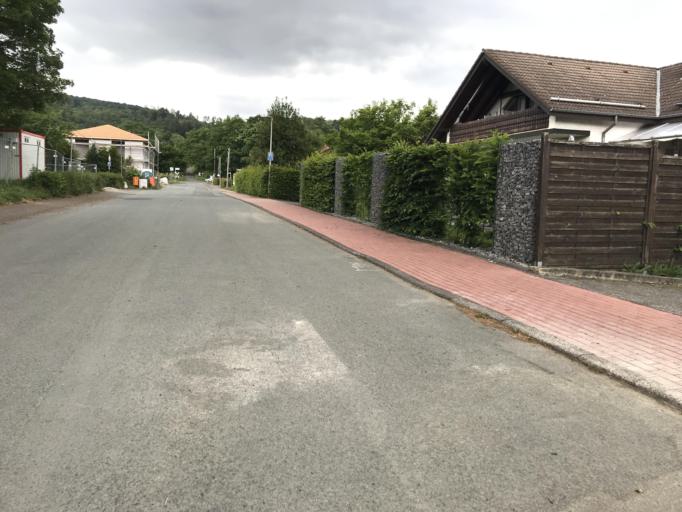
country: DE
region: Hesse
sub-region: Regierungsbezirk Kassel
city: Martinhagen
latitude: 51.2883
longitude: 9.3487
